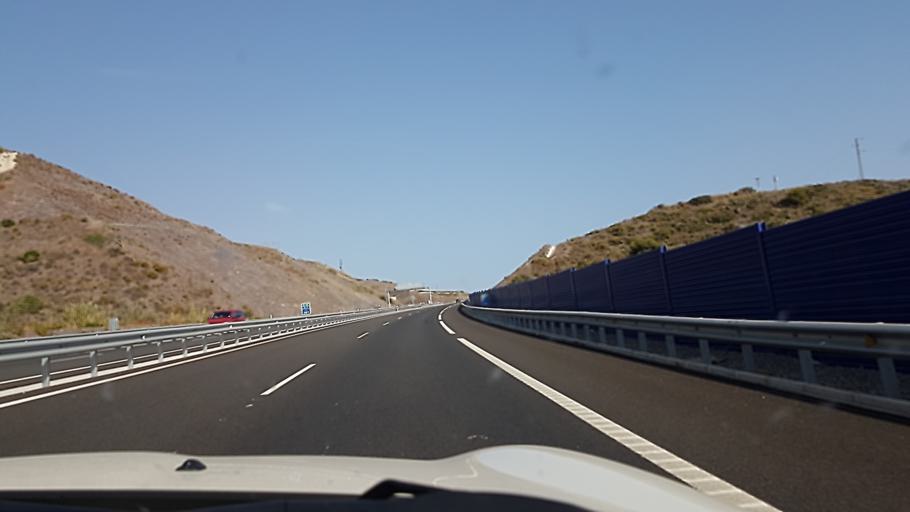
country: ES
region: Andalusia
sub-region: Provincia de Granada
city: Albunol
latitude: 36.7570
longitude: -3.2365
